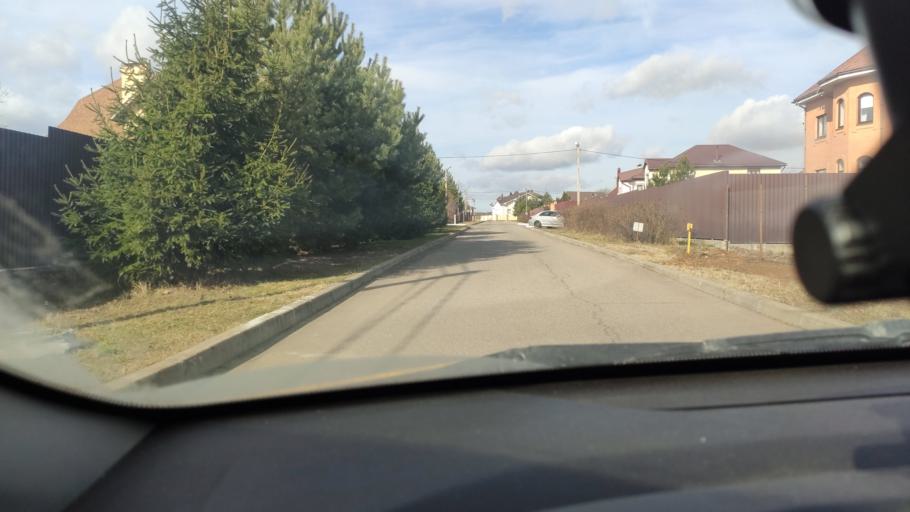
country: RU
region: Moskovskaya
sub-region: Podol'skiy Rayon
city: Podol'sk
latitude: 55.3930
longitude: 37.6265
